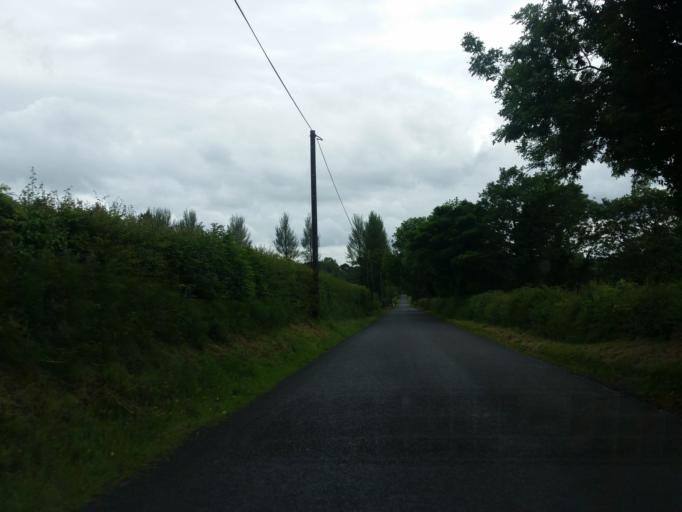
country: GB
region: Northern Ireland
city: Lisnaskea
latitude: 54.2559
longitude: -7.3827
